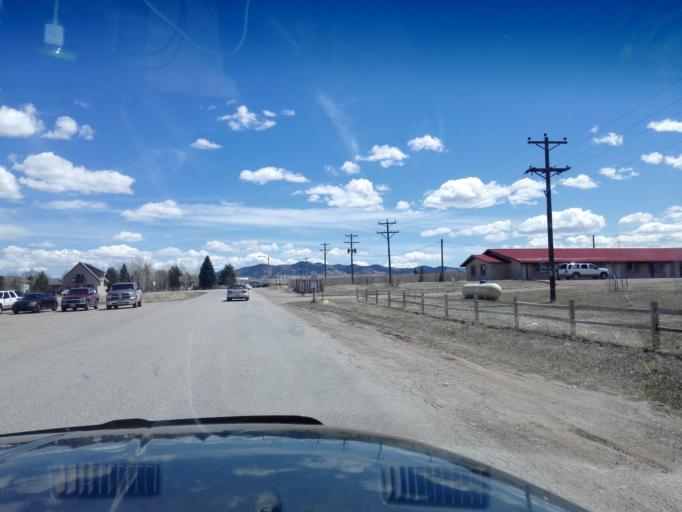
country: US
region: Colorado
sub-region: Custer County
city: Westcliffe
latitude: 38.1309
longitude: -105.4636
